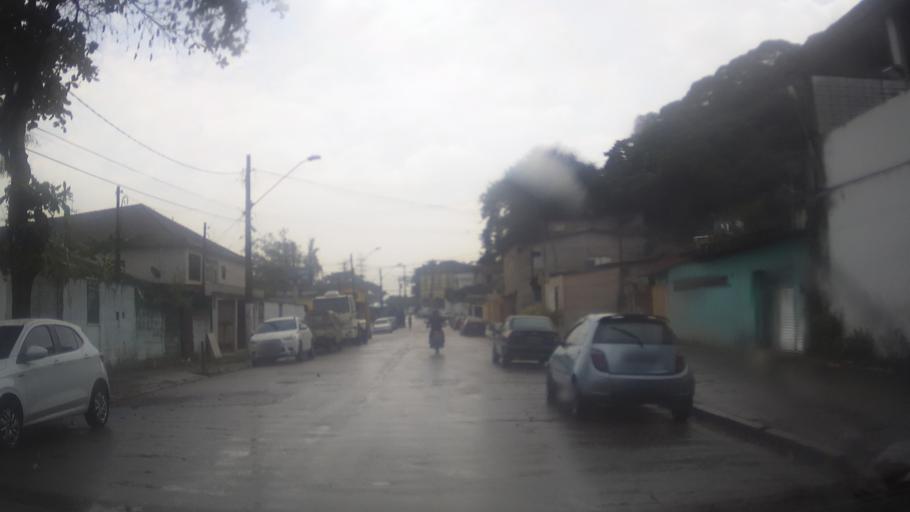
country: BR
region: Sao Paulo
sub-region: Sao Vicente
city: Sao Vicente
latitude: -23.9414
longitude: -46.3637
